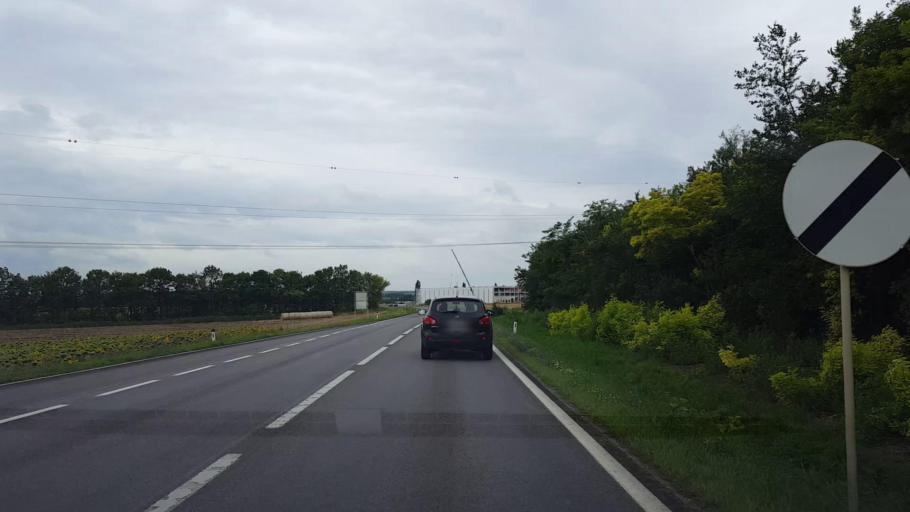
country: AT
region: Lower Austria
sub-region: Politischer Bezirk Bruck an der Leitha
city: Enzersdorf an der Fischa
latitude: 48.0627
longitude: 16.6171
